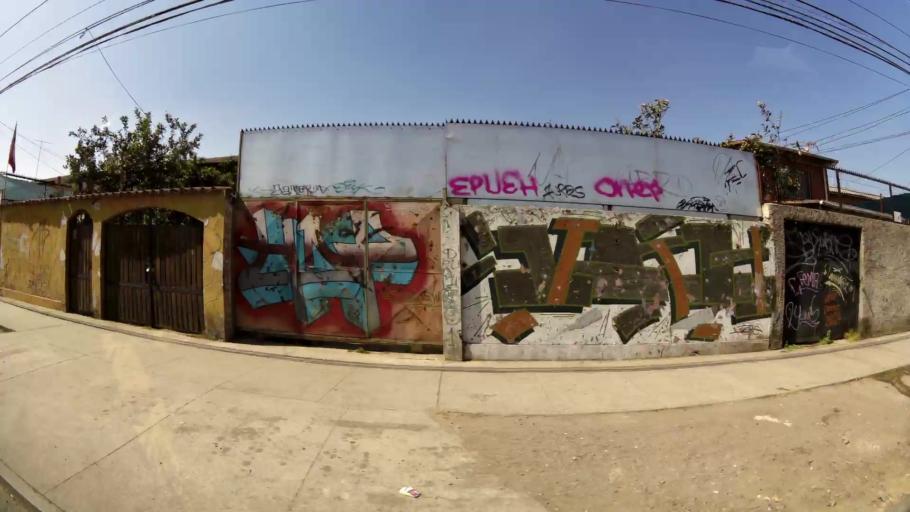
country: CL
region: Santiago Metropolitan
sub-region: Provincia de Santiago
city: Lo Prado
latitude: -33.4109
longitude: -70.6927
